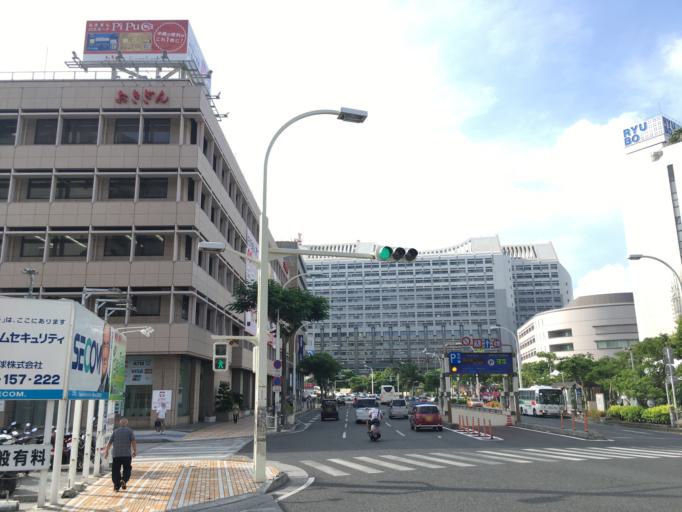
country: JP
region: Okinawa
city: Naha-shi
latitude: 26.2148
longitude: 127.6798
